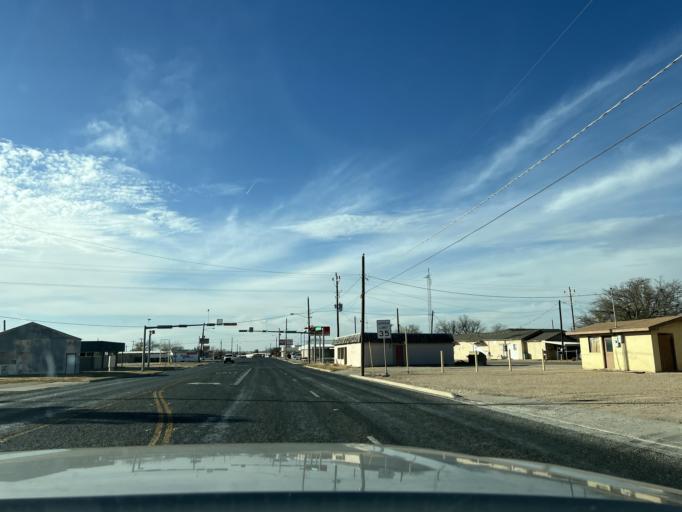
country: US
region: Texas
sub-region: Scurry County
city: Snyder
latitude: 32.7156
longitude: -100.9009
